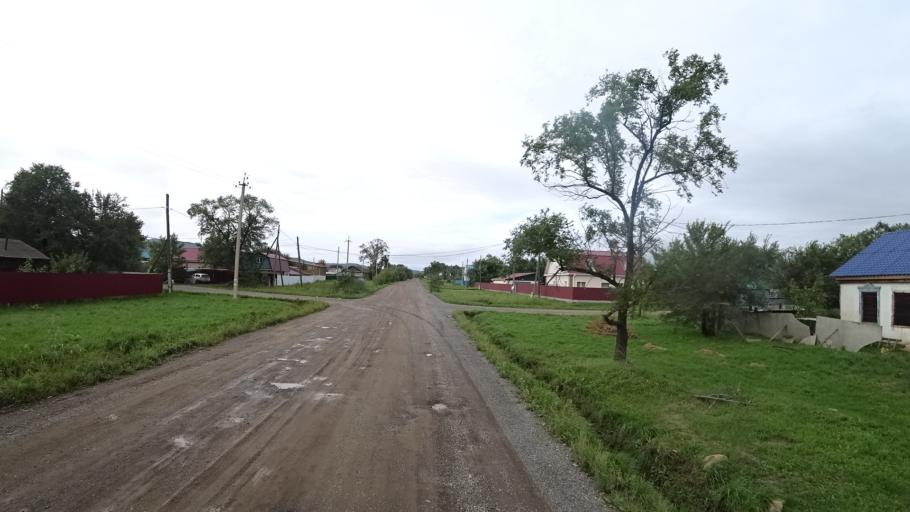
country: RU
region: Primorskiy
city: Chernigovka
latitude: 44.3346
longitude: 132.5771
